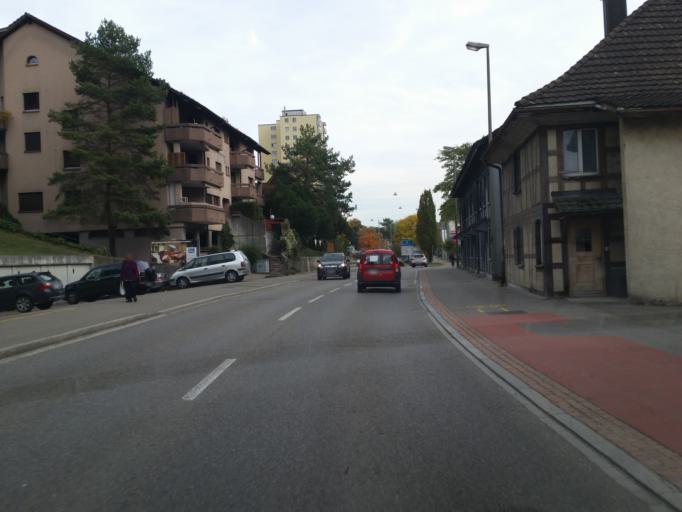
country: CH
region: Zurich
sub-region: Bezirk Winterthur
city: Wuelflingen (Kreis 6) / Haerti
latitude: 47.5160
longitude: 8.6806
